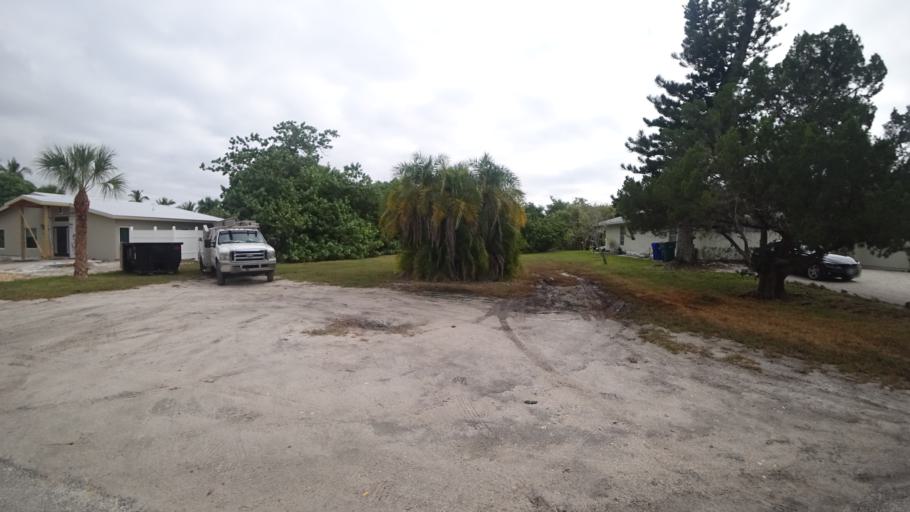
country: US
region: Florida
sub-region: Manatee County
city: Longboat Key
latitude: 27.4292
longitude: -82.6737
